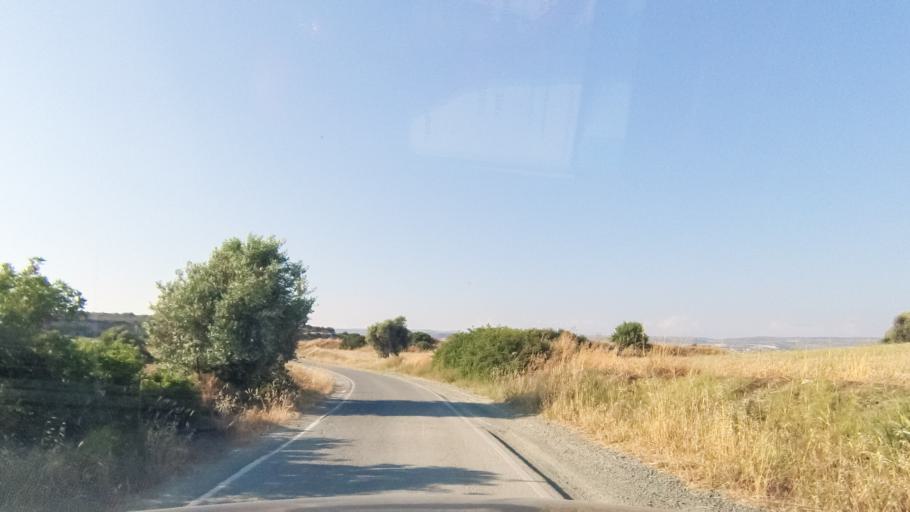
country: CY
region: Limassol
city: Pissouri
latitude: 34.6709
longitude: 32.7669
